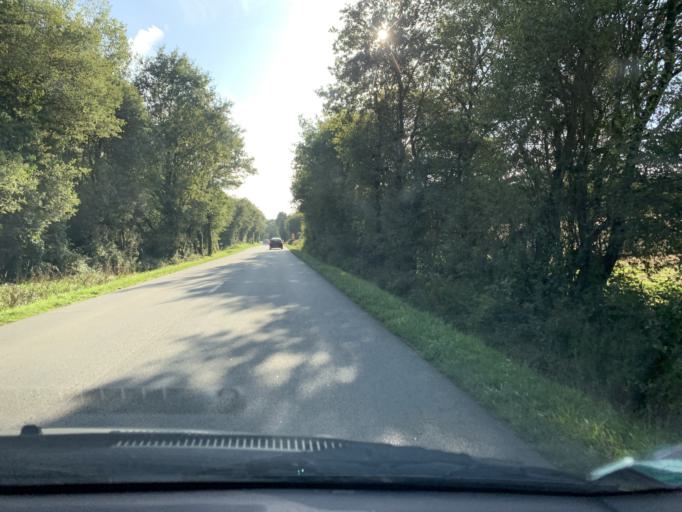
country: FR
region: Brittany
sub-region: Departement du Morbihan
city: Surzur
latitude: 47.5657
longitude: -2.6776
